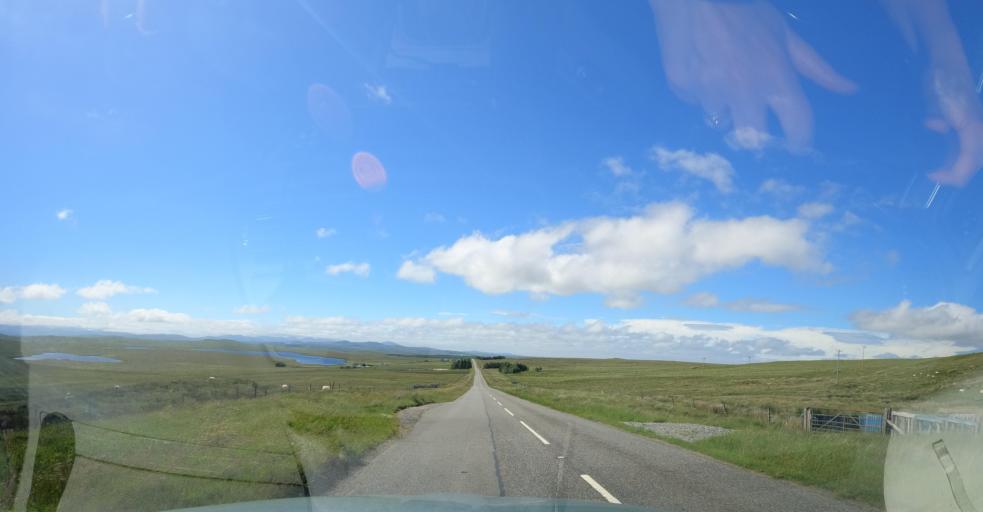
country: GB
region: Scotland
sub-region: Eilean Siar
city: Stornoway
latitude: 58.1727
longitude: -6.5907
